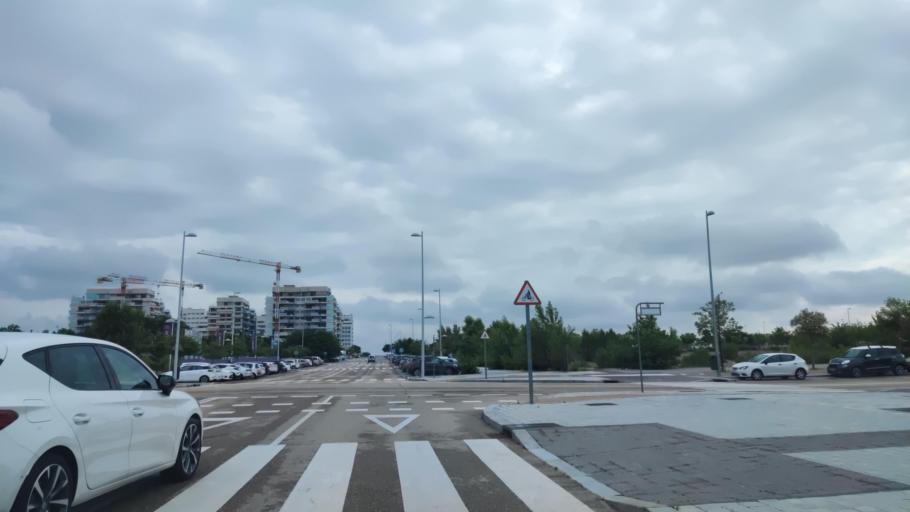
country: ES
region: Madrid
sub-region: Provincia de Madrid
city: Barajas de Madrid
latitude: 40.4874
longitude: -3.6065
